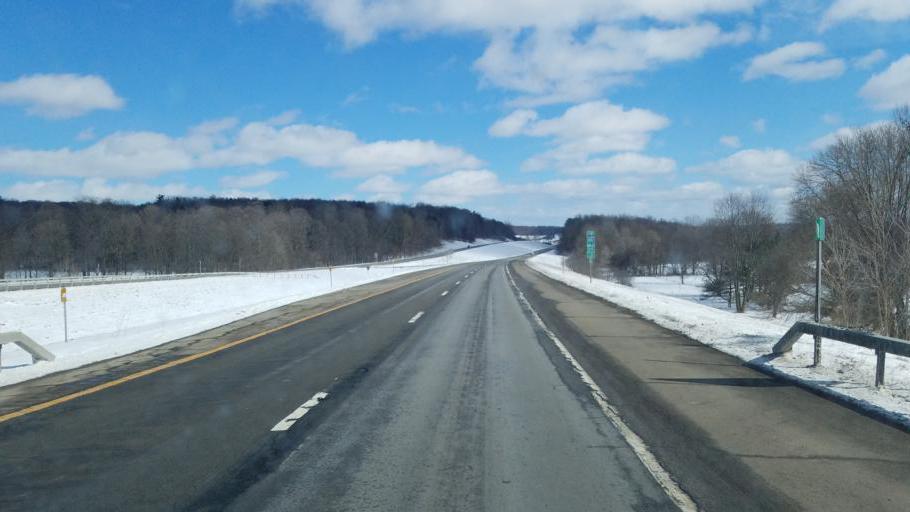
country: US
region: New York
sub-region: Chautauqua County
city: Celoron
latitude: 42.1280
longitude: -79.2948
